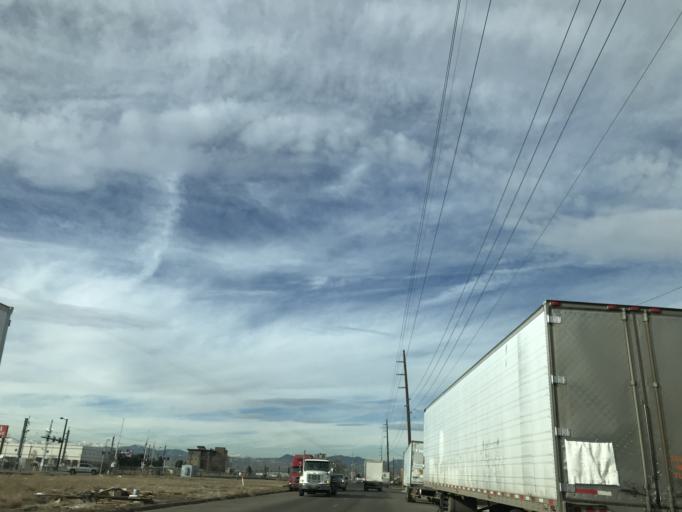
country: US
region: Colorado
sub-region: Adams County
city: Commerce City
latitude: 39.7738
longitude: -104.9112
